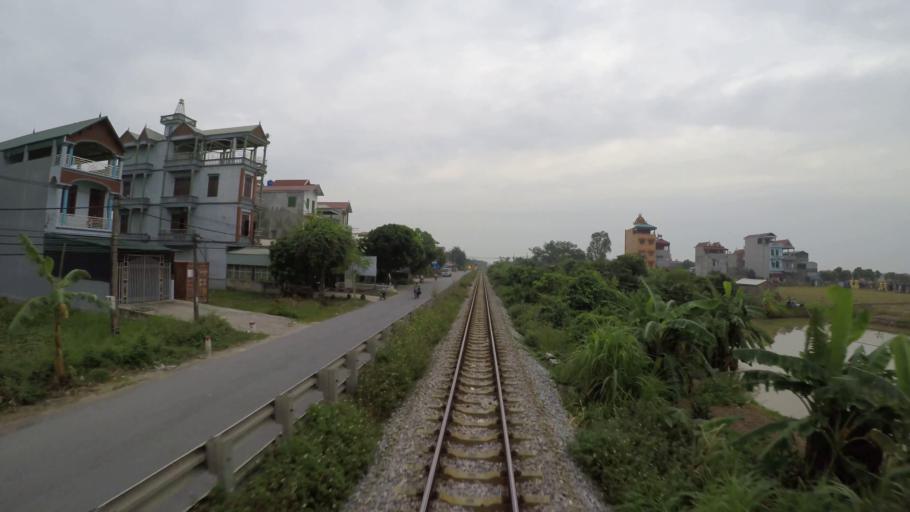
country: VN
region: Hung Yen
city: Ban Yen Nhan
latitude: 20.9663
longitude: 106.1093
